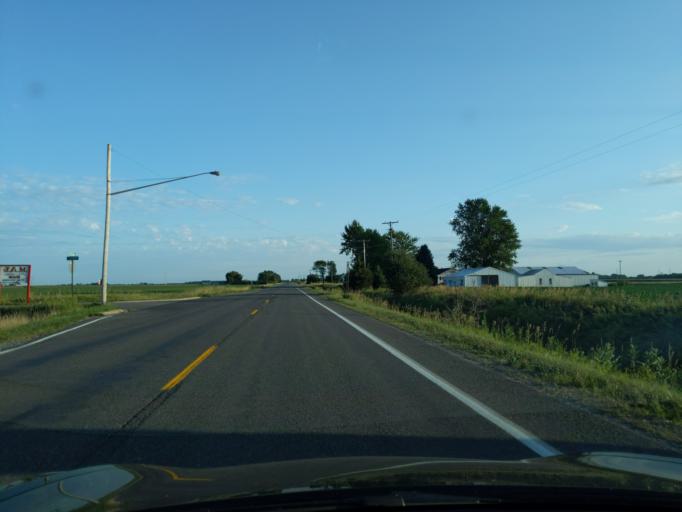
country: US
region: Michigan
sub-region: Gratiot County
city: Breckenridge
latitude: 43.4964
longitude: -84.3699
